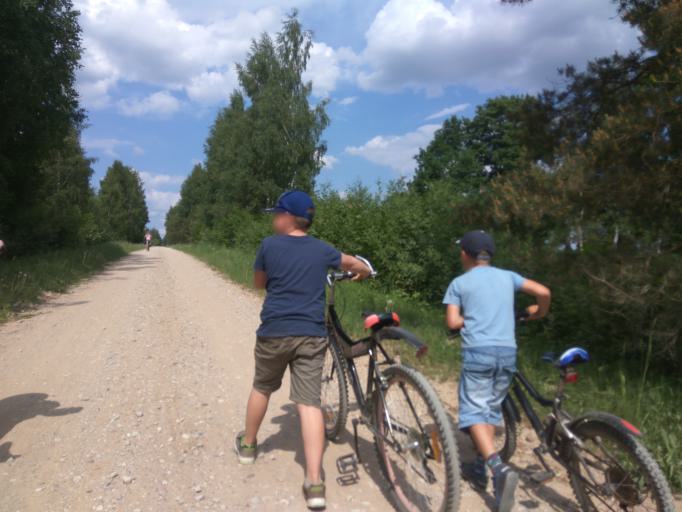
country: LV
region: Kuldigas Rajons
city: Kuldiga
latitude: 56.9097
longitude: 21.9501
